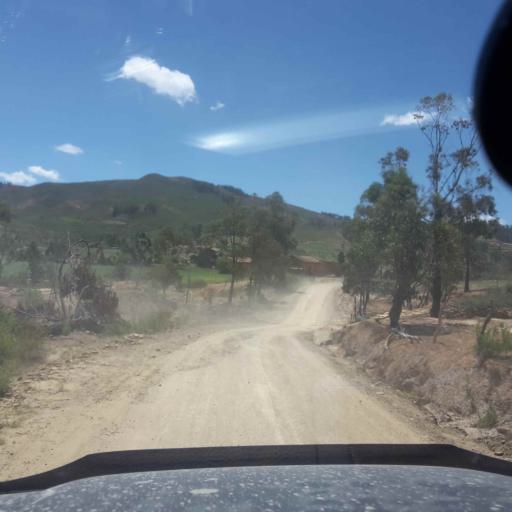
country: BO
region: Cochabamba
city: Totora
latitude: -17.7637
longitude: -65.2341
